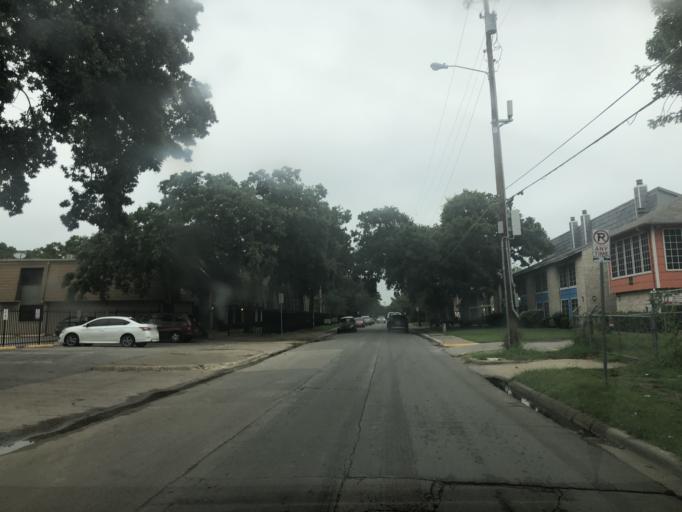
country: US
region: Texas
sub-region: Dallas County
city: Farmers Branch
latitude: 32.8594
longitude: -96.8763
